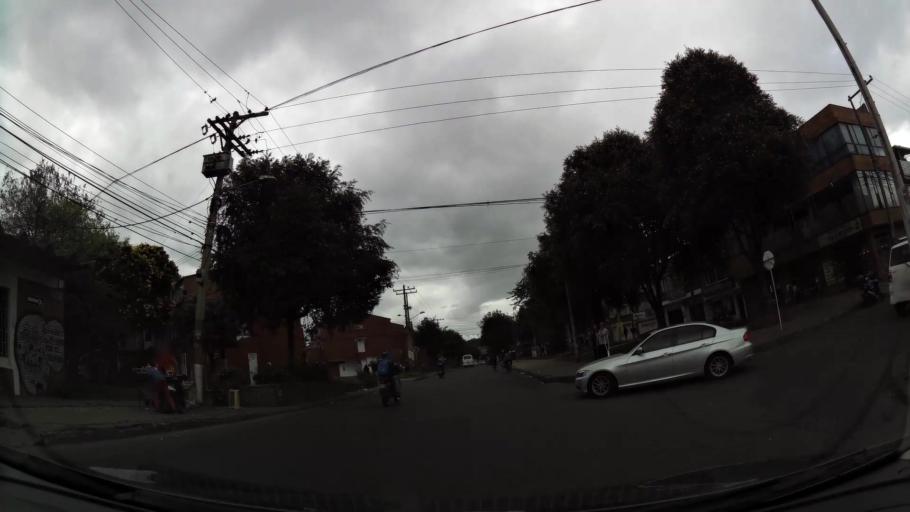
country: CO
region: Bogota D.C.
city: Barrio San Luis
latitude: 4.7097
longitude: -74.1021
